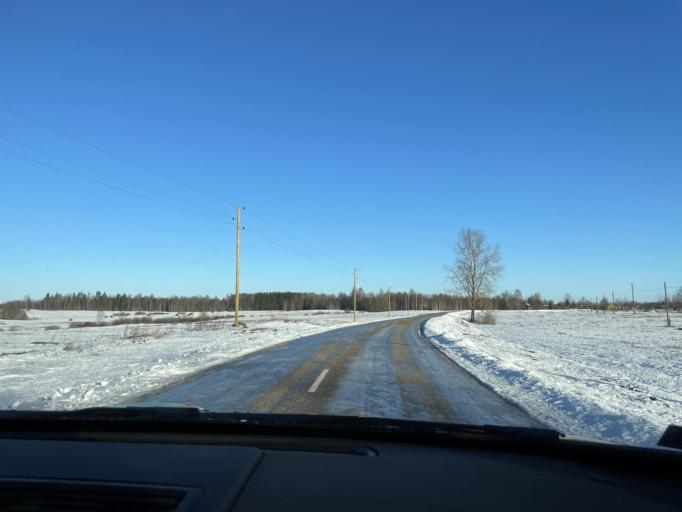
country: LV
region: Ludzas Rajons
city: Ludza
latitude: 56.4611
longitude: 27.5704
